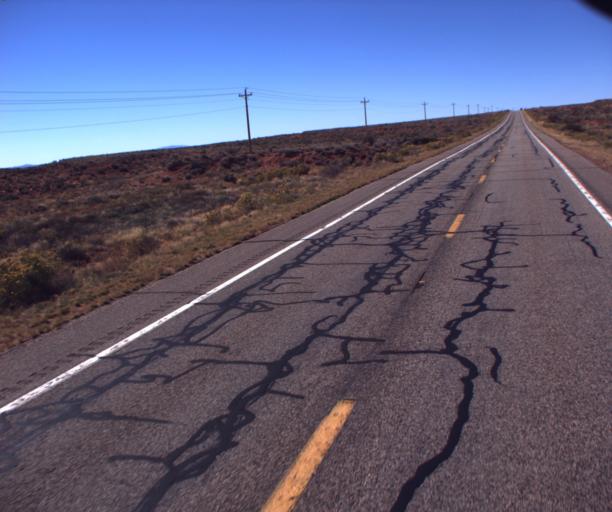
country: US
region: Arizona
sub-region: Coconino County
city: Fredonia
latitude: 36.8623
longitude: -112.7129
